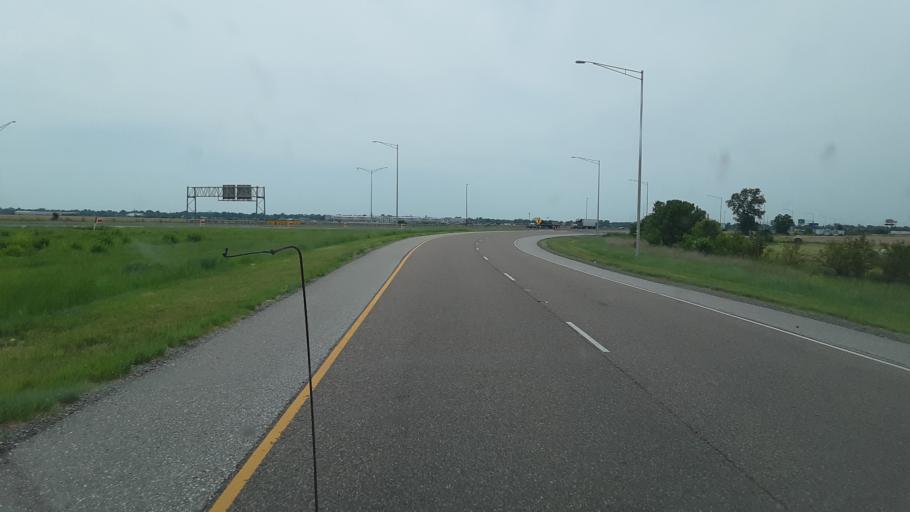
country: US
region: Illinois
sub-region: Madison County
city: Mitchell
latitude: 38.7582
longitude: -90.0500
